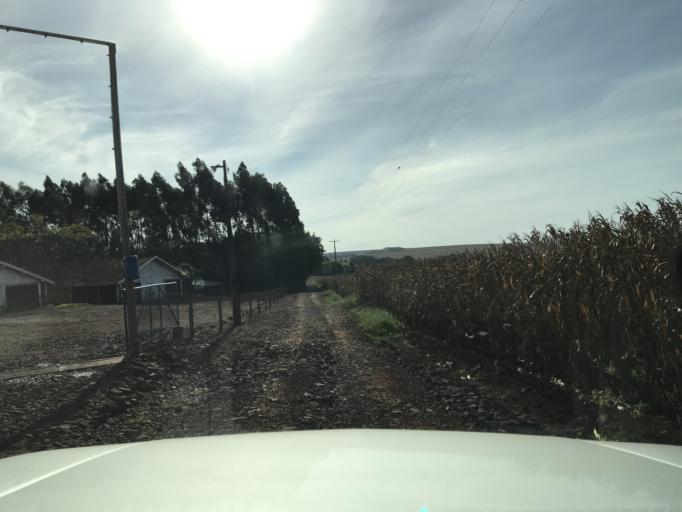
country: BR
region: Parana
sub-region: Palotina
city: Palotina
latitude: -24.2581
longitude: -53.7488
